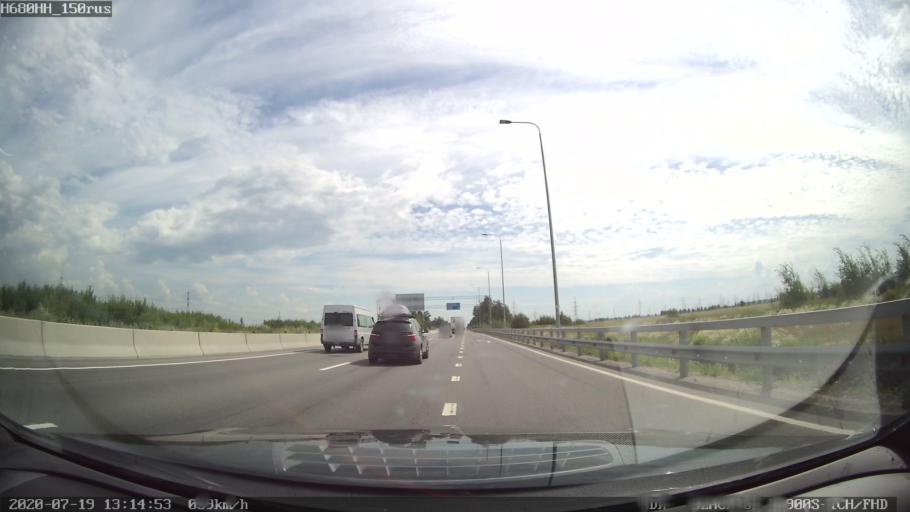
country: RU
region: St.-Petersburg
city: Kolpino
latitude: 59.7297
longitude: 30.5315
